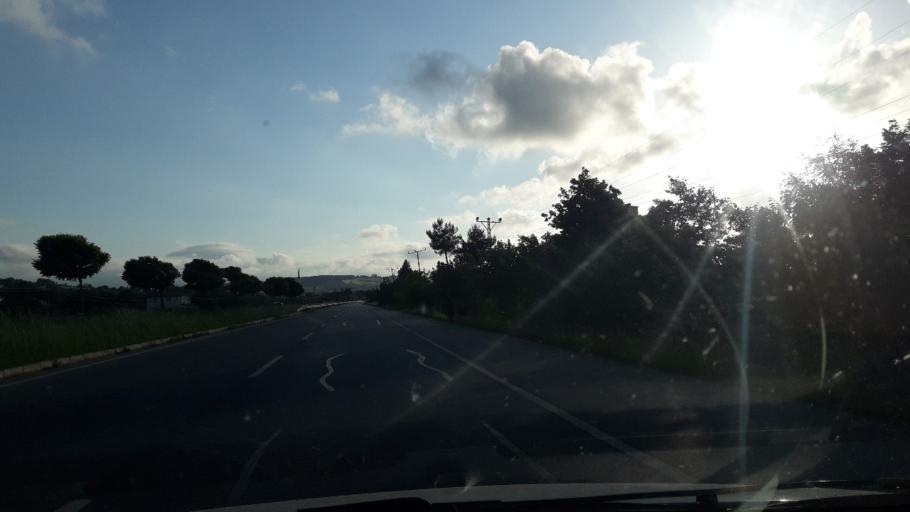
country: TR
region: Samsun
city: Bafra
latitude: 41.6008
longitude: 35.7897
